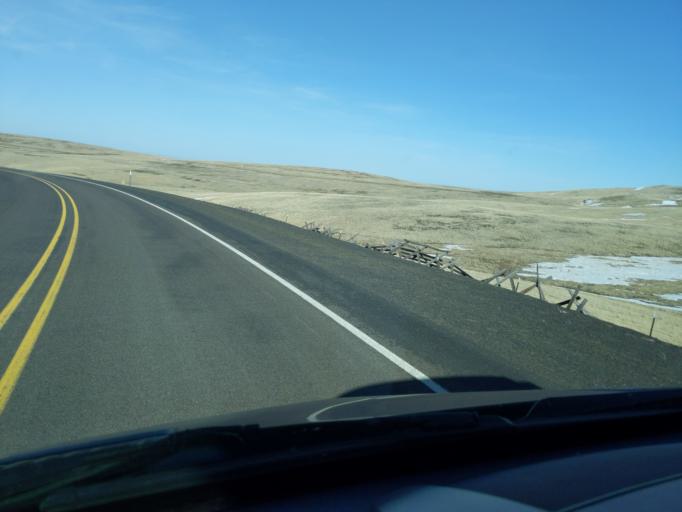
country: US
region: Oregon
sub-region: Umatilla County
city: Pilot Rock
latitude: 45.3057
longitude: -119.0039
